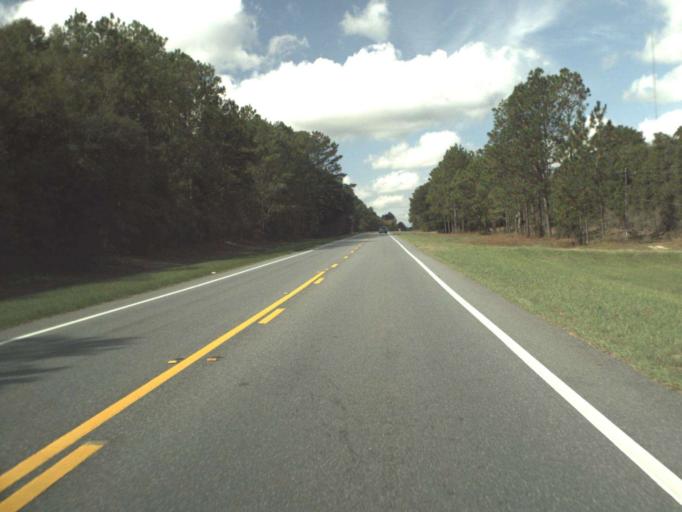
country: US
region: Florida
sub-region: Jackson County
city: Marianna
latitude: 30.7359
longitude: -85.1051
